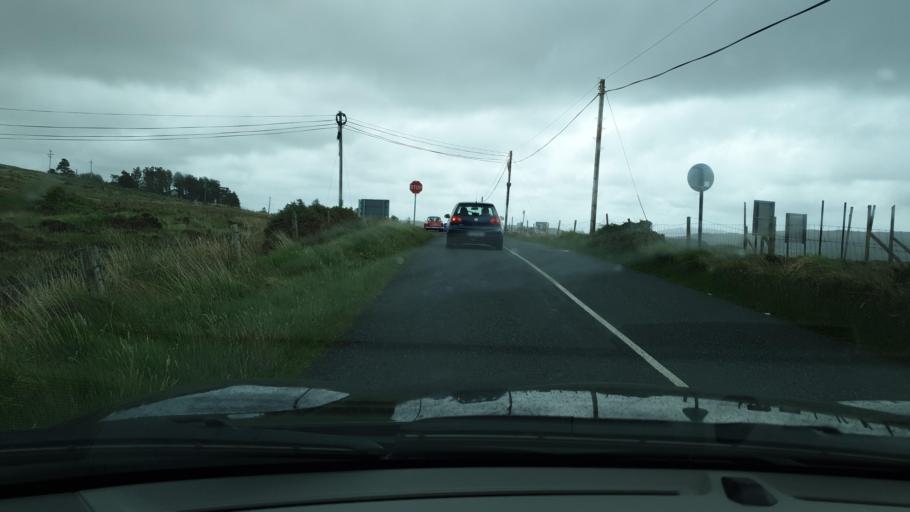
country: IE
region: Connaught
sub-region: County Galway
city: Clifden
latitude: 53.5238
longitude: -10.0491
